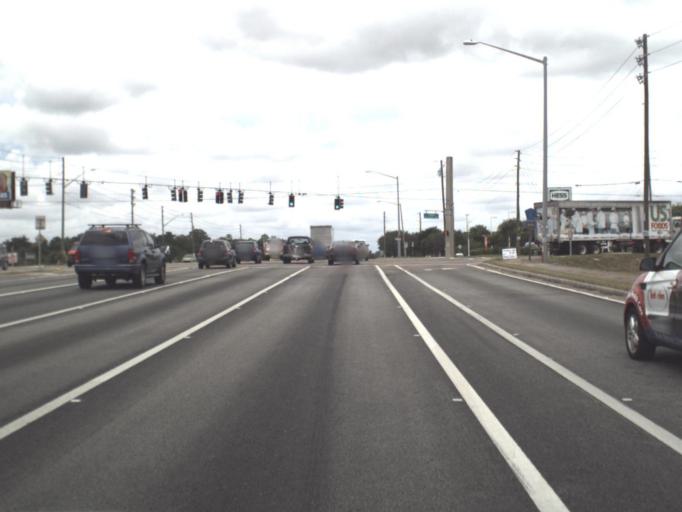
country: US
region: Florida
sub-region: Pasco County
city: Trinity
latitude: 28.2062
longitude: -82.6652
